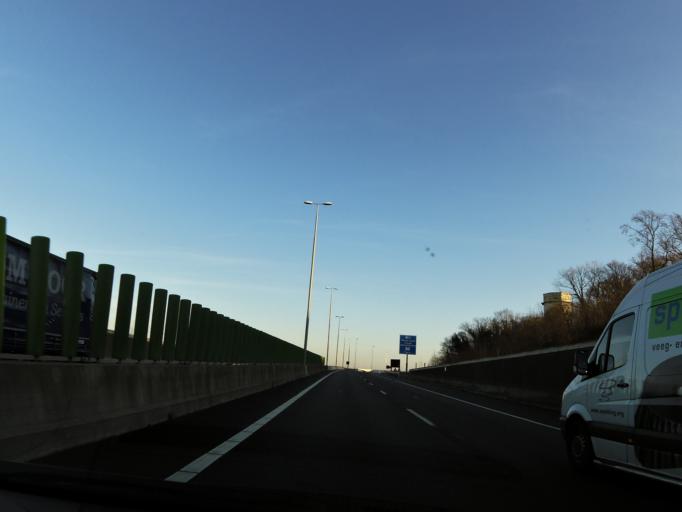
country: NL
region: Limburg
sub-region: Gemeente Venlo
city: Tegelen
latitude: 51.3389
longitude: 6.1528
